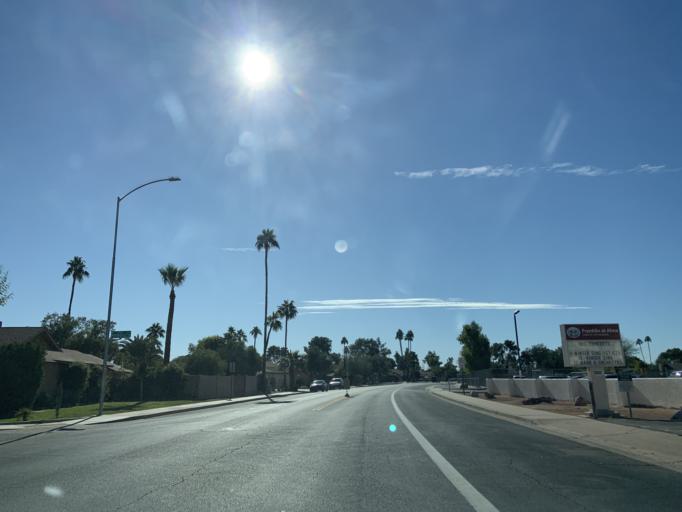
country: US
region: Arizona
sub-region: Maricopa County
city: San Carlos
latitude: 33.3701
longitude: -111.8612
